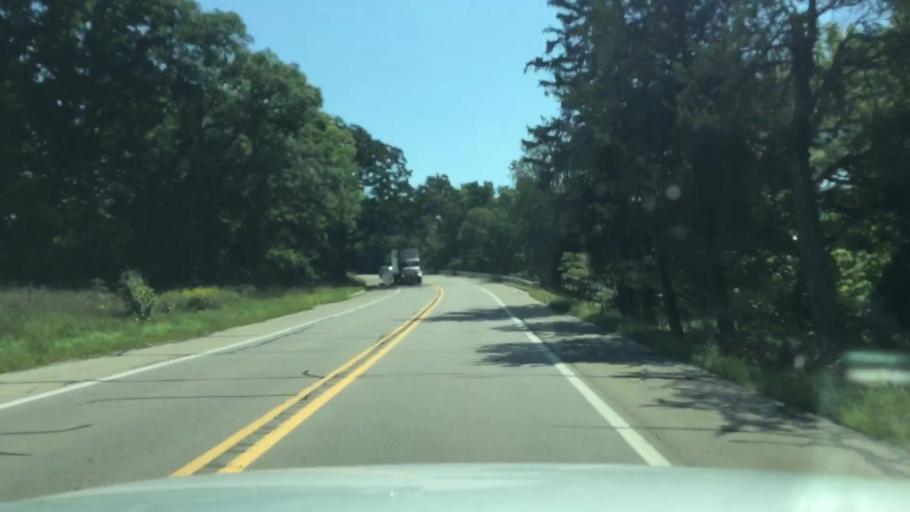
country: US
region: Michigan
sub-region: Jackson County
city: Brooklyn
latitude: 42.0604
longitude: -84.1818
